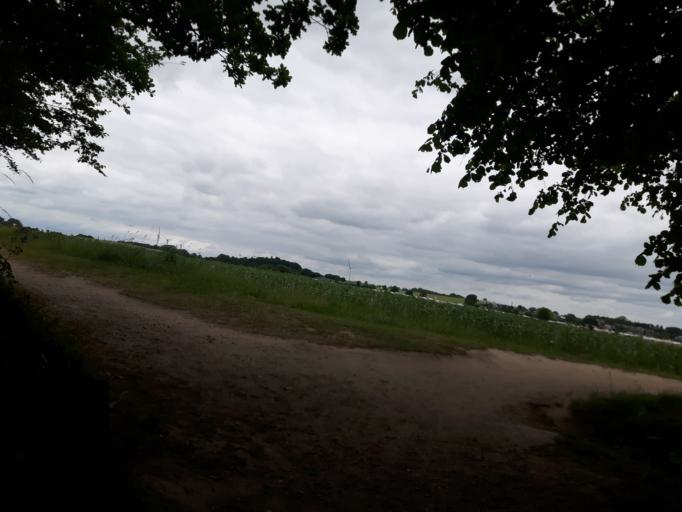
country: DE
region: Schleswig-Holstein
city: Schashagen
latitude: 54.1177
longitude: 10.9240
